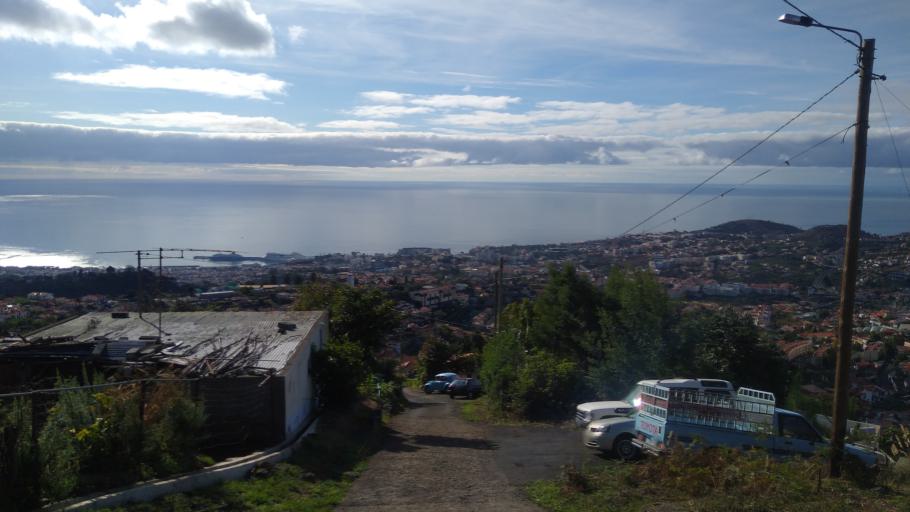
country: PT
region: Madeira
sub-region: Funchal
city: Nossa Senhora do Monte
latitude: 32.6769
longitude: -16.9252
